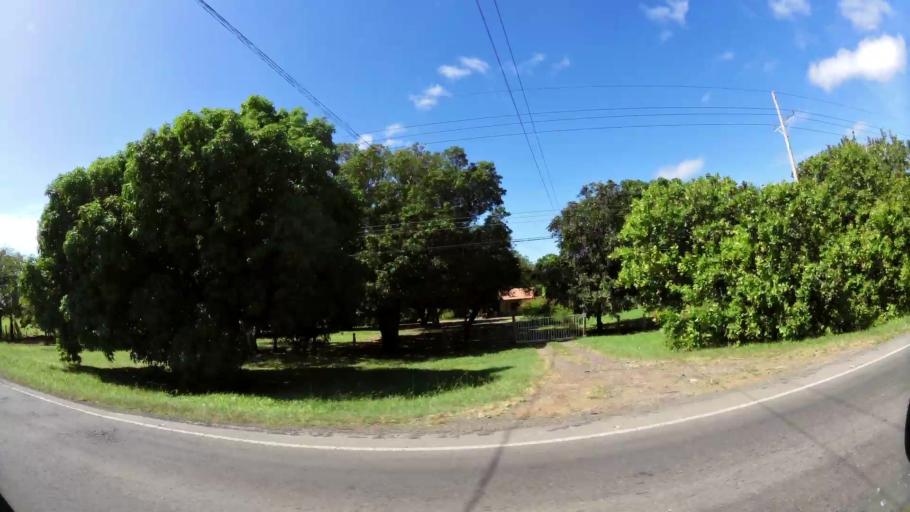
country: CR
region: Guanacaste
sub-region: Canton de Canas
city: Canas
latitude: 10.3977
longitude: -85.0807
